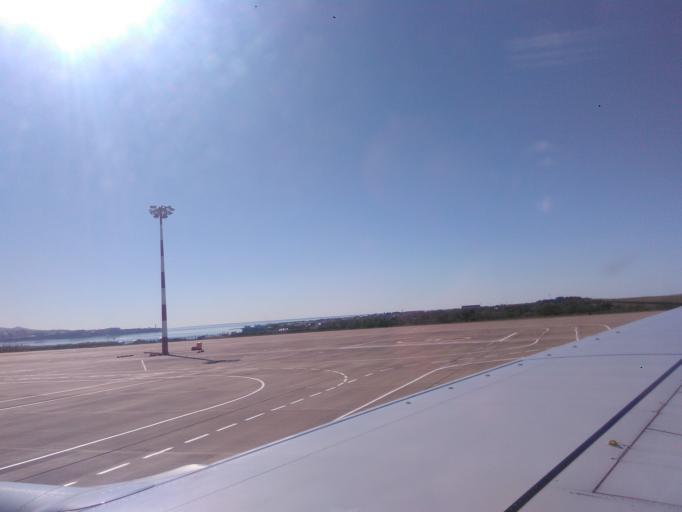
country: RU
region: Krasnodarskiy
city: Gelendzhik
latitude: 44.5941
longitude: 38.0204
